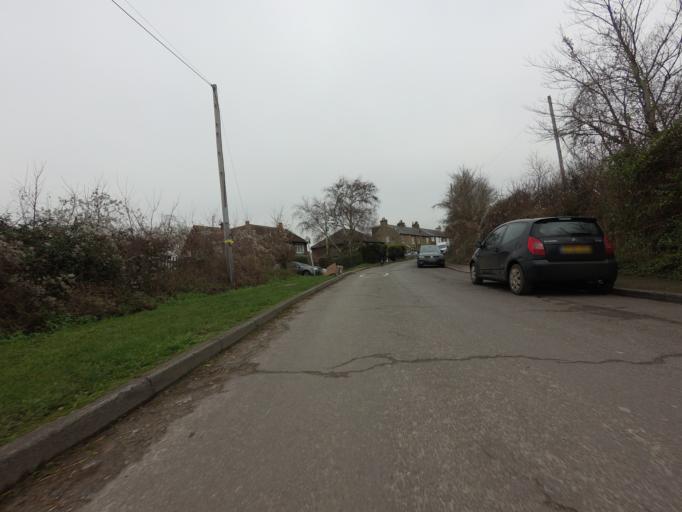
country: GB
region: England
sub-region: Kent
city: Eynsford
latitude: 51.3909
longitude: 0.2440
